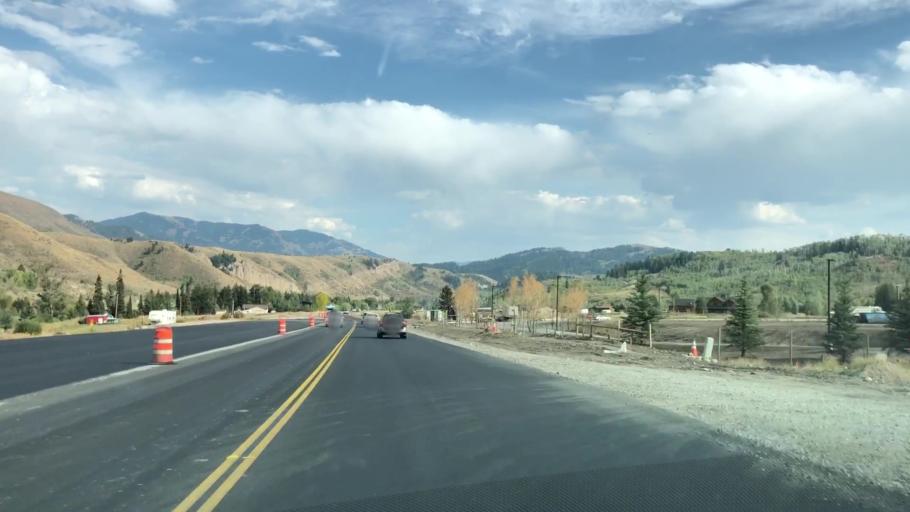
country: US
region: Wyoming
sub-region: Teton County
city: South Park
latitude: 43.3718
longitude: -110.7423
